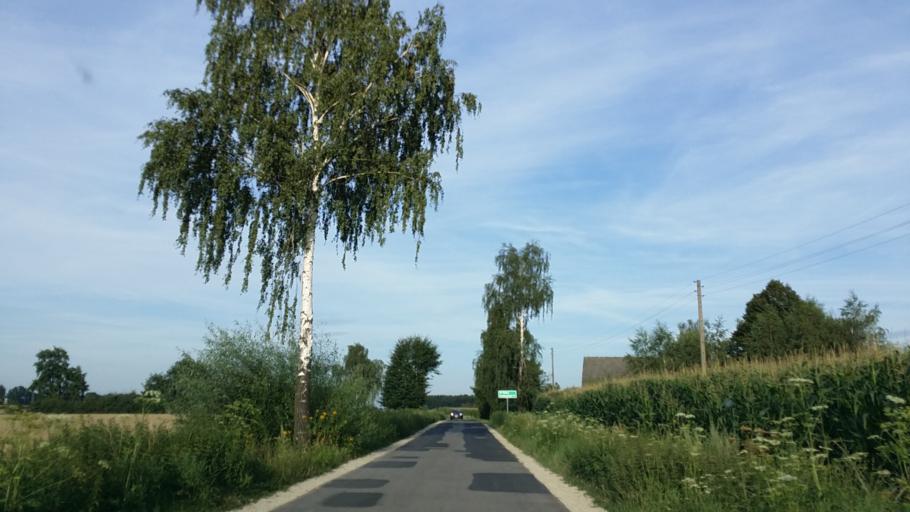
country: PL
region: Lesser Poland Voivodeship
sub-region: Powiat oswiecimski
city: Przeciszow
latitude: 49.9916
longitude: 19.3995
